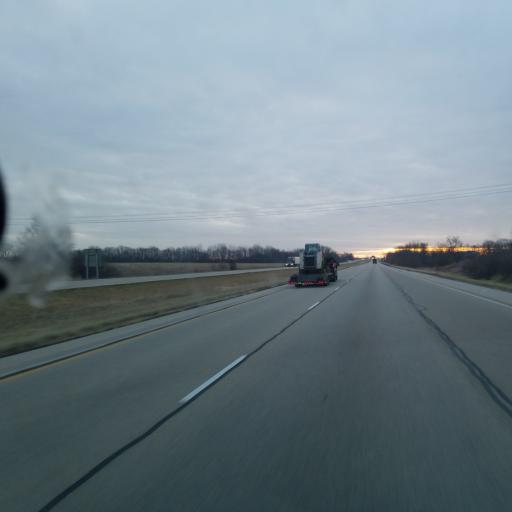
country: US
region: Illinois
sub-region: McLean County
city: Downs
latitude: 40.3875
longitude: -88.8717
